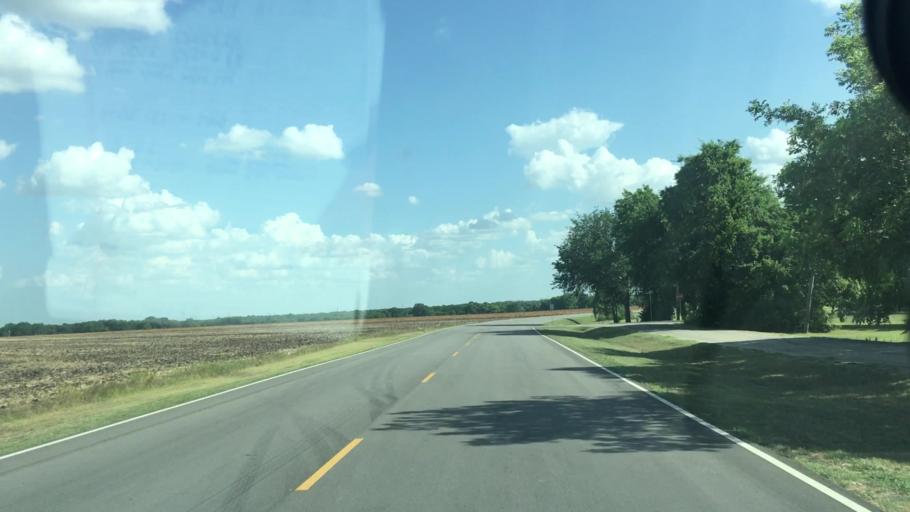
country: US
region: Texas
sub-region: Dallas County
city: Lancaster
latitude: 32.5943
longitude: -96.7479
